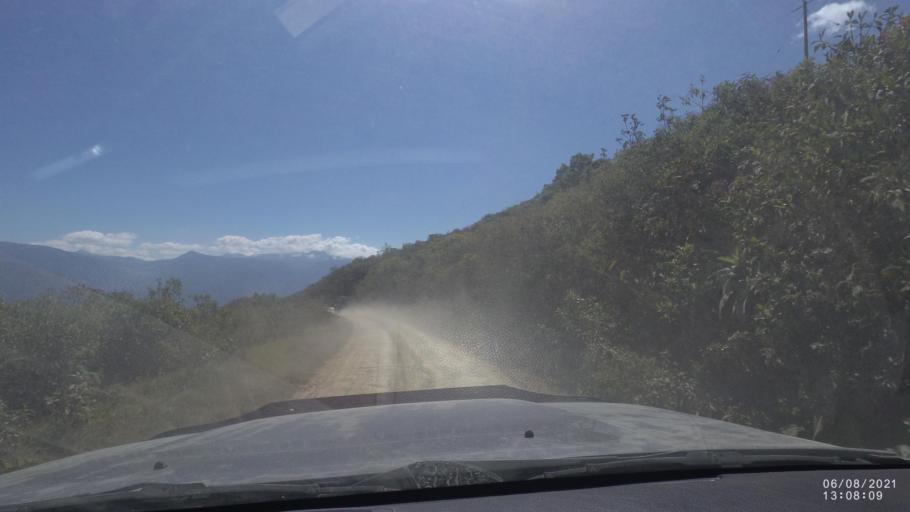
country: BO
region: La Paz
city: Quime
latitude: -16.7299
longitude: -66.7058
